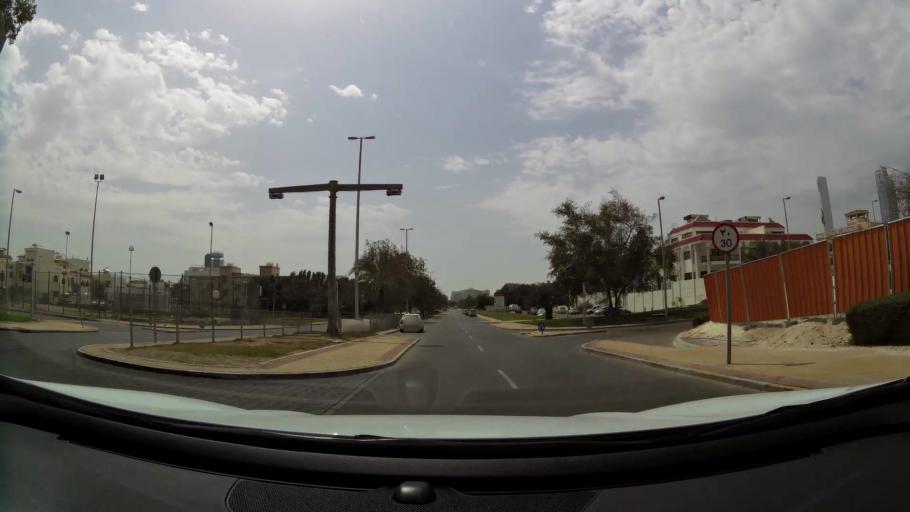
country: AE
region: Abu Dhabi
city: Abu Dhabi
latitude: 24.4633
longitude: 54.3394
